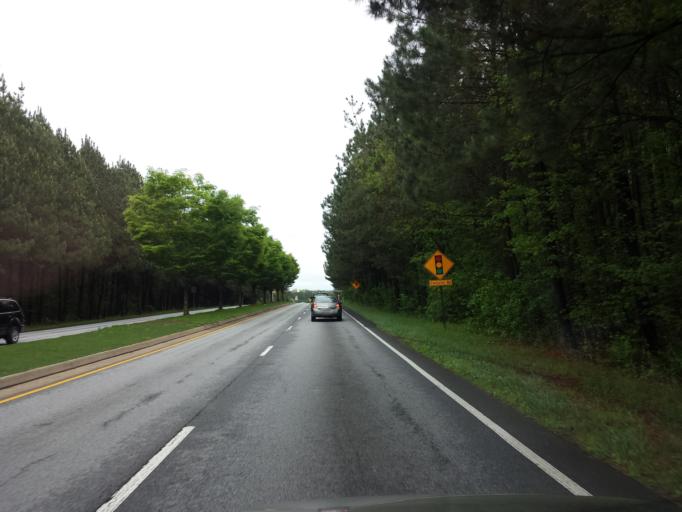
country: US
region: Georgia
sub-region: Cobb County
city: Smyrna
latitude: 33.8452
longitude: -84.5415
